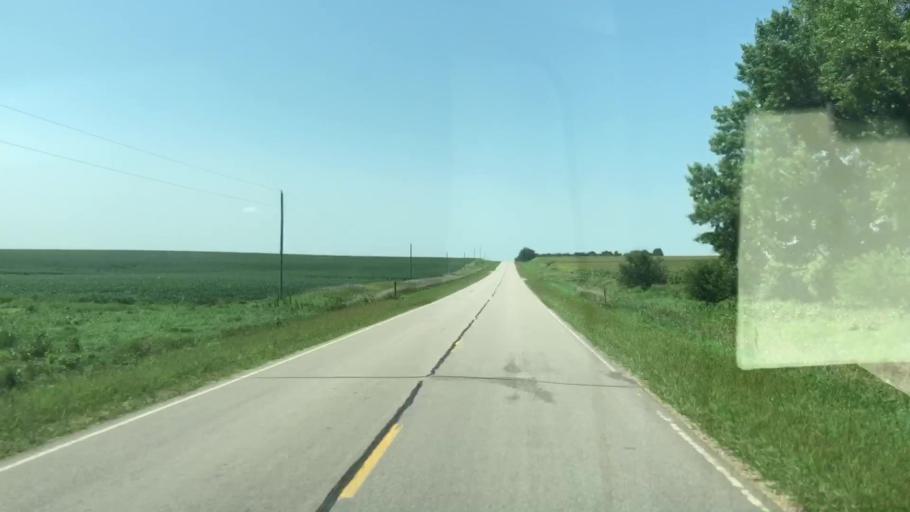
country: US
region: Iowa
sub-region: O'Brien County
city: Sanborn
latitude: 43.2443
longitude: -95.7294
